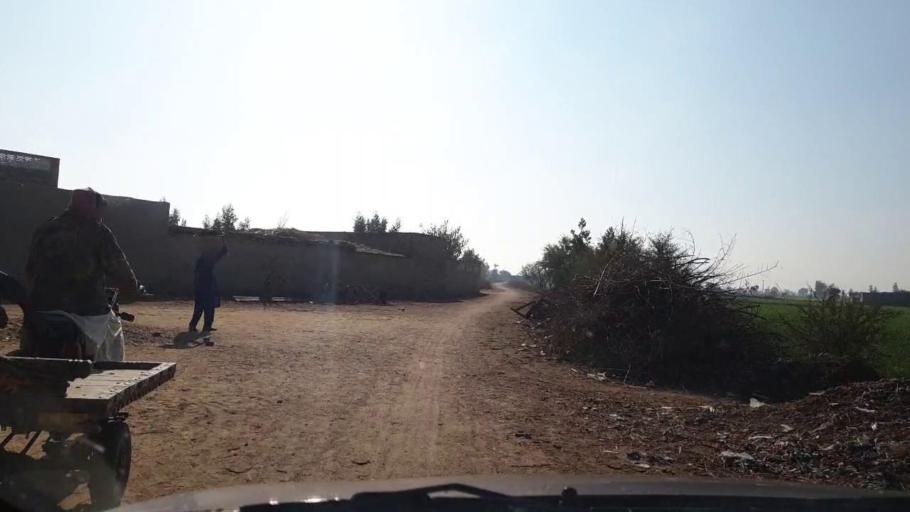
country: PK
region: Sindh
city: Sinjhoro
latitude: 26.0021
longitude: 68.7773
